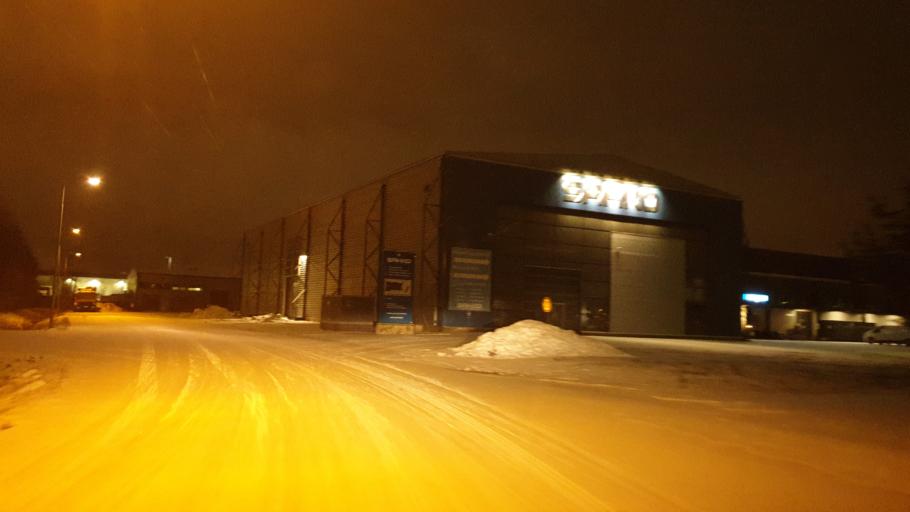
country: FI
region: Northern Ostrobothnia
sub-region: Oulu
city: Oulu
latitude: 64.9933
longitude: 25.4514
